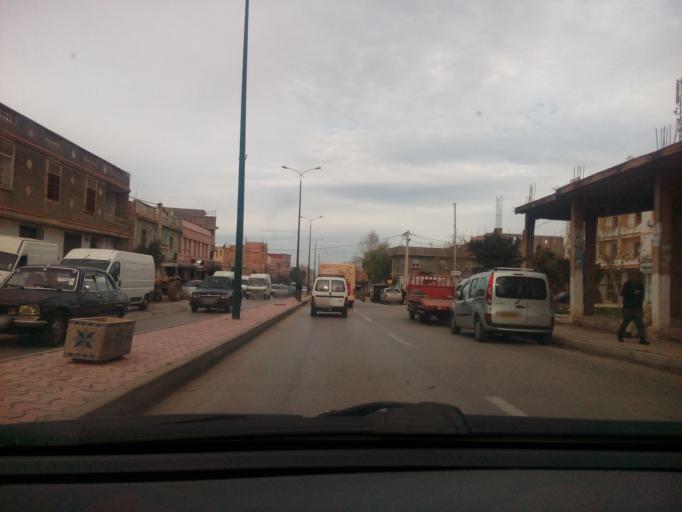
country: DZ
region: Tlemcen
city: Mansoura
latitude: 34.8819
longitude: -1.3498
